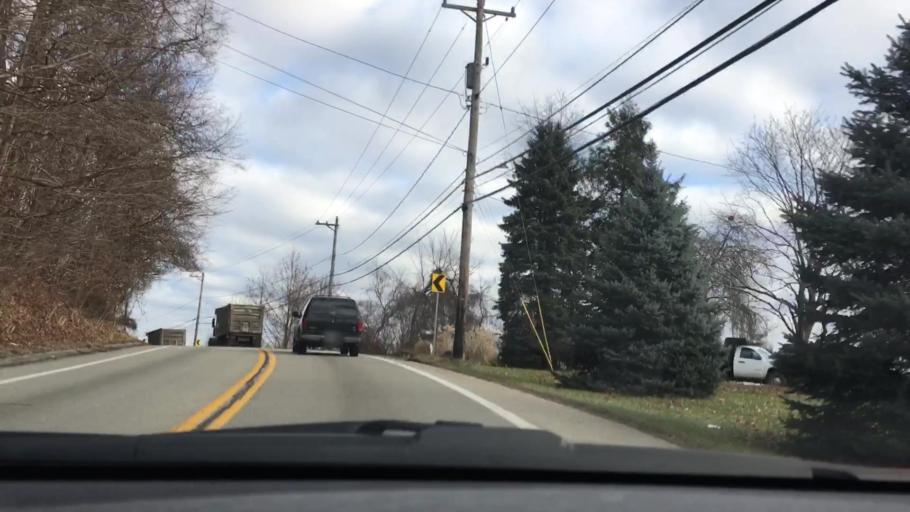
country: US
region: Pennsylvania
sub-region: Westmoreland County
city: Trafford
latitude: 40.3729
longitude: -79.7763
